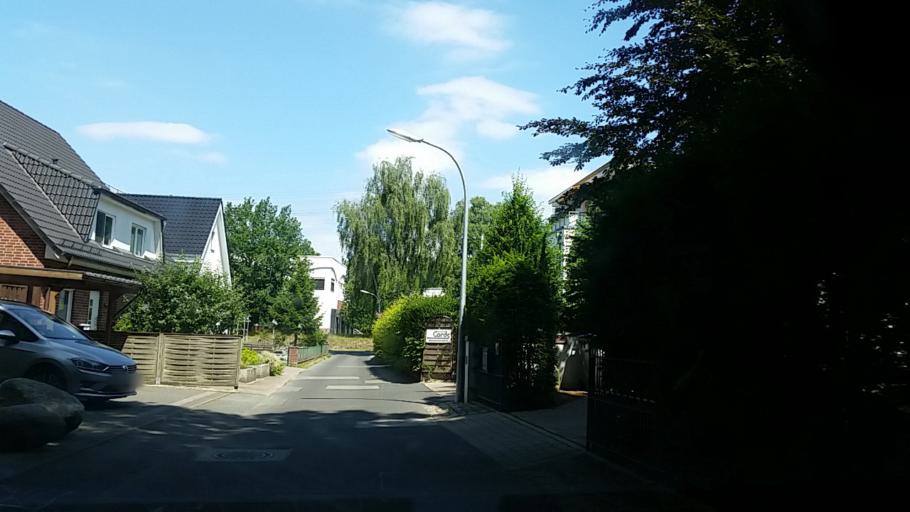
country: DE
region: Schleswig-Holstein
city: Wedel
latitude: 53.5802
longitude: 9.7671
